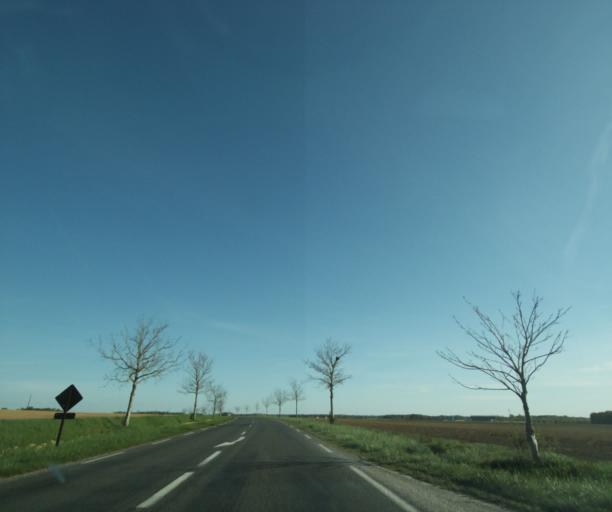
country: FR
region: Ile-de-France
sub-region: Departement de Seine-et-Marne
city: Nangis
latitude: 48.5546
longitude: 2.9969
